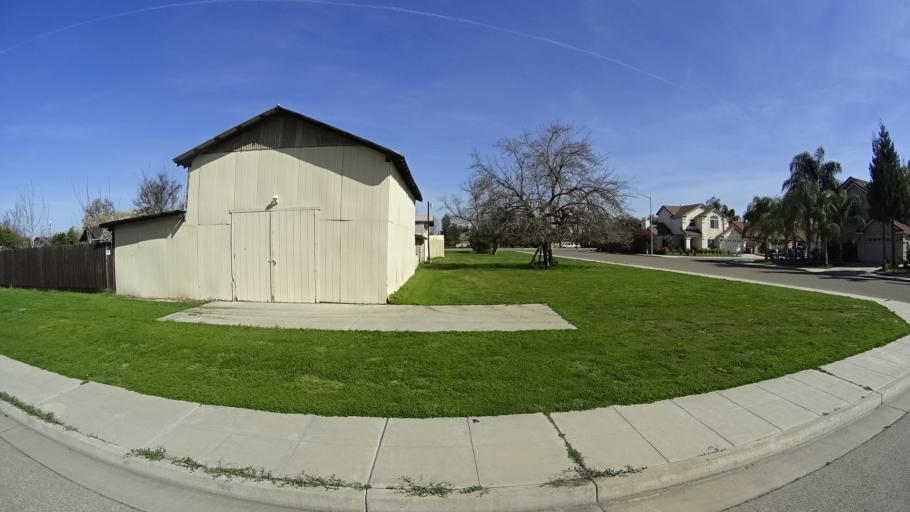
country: US
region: California
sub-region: Fresno County
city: Clovis
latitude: 36.8480
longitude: -119.7310
